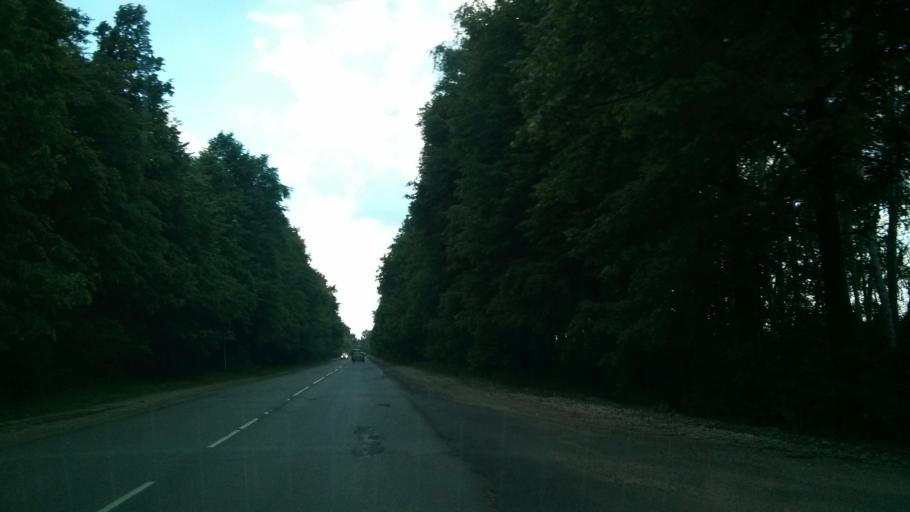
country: RU
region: Vladimir
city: Murom
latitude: 55.5400
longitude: 41.9811
